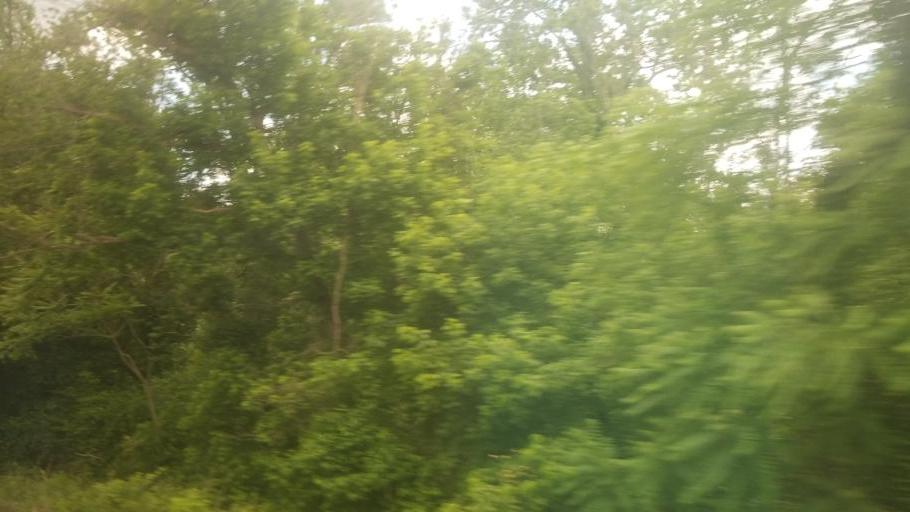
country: US
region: Maryland
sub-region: Frederick County
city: Brunswick
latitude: 39.3077
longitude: -77.6124
